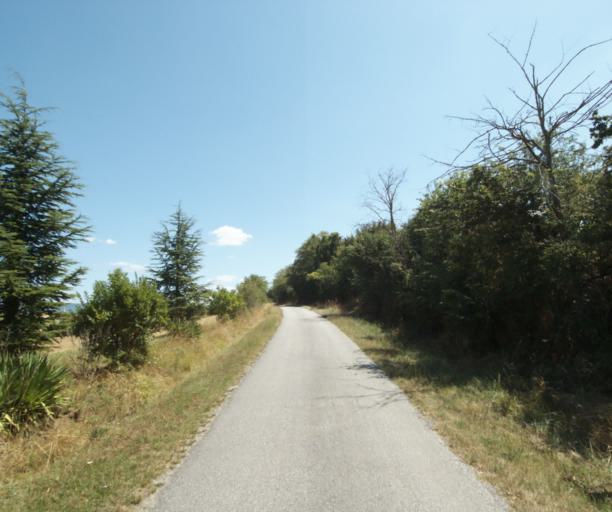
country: FR
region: Midi-Pyrenees
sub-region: Departement de la Haute-Garonne
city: Saint-Felix-Lauragais
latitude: 43.4637
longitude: 1.8892
